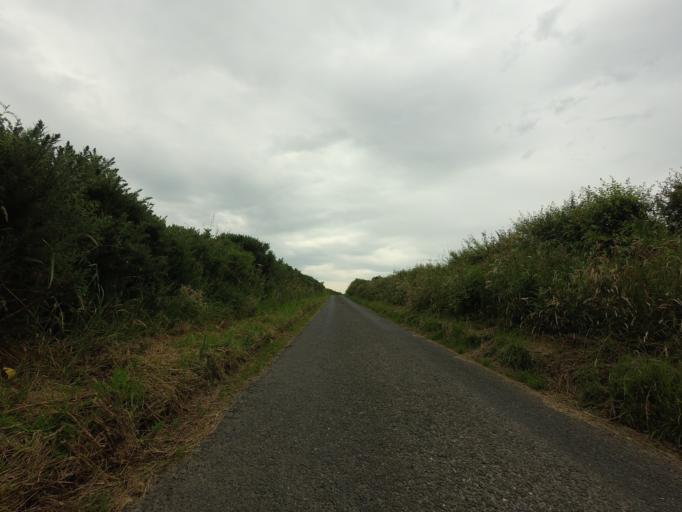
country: GB
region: Scotland
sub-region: Aberdeenshire
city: Whitehills
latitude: 57.6712
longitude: -2.5982
